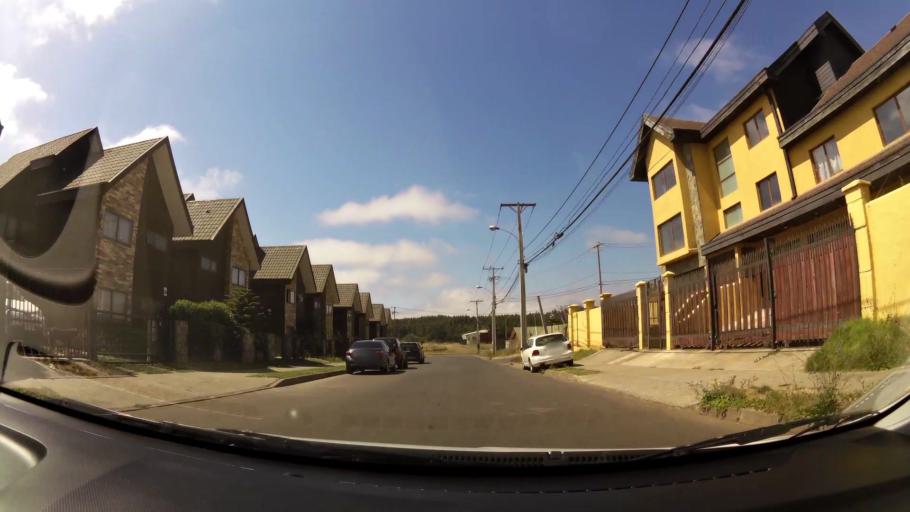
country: CL
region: Biobio
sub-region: Provincia de Concepcion
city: Concepcion
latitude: -36.7778
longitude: -73.0430
